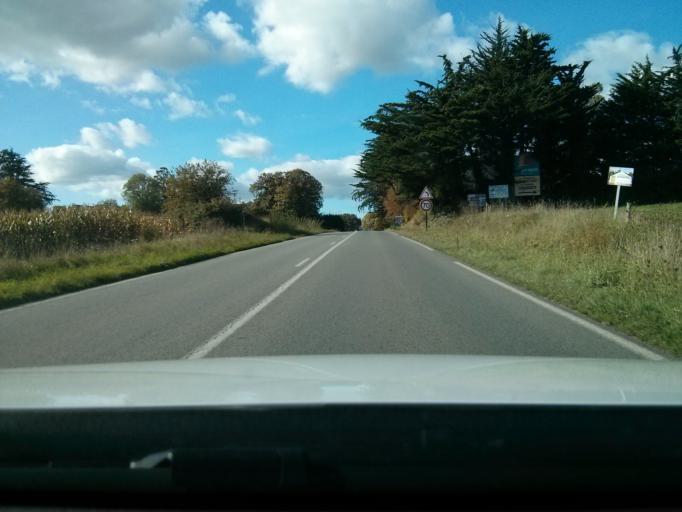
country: FR
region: Brittany
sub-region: Departement des Cotes-d'Armor
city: Ploubalay
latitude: 48.5765
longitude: -2.1714
